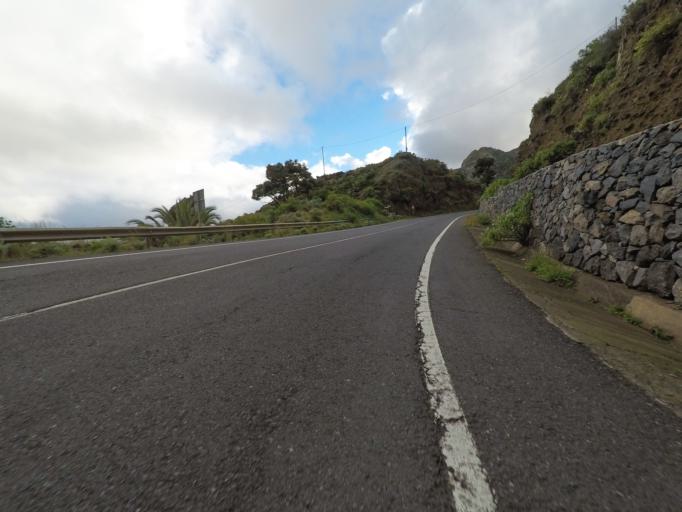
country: ES
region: Canary Islands
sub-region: Provincia de Santa Cruz de Tenerife
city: Hermigua
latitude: 28.1314
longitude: -17.1828
